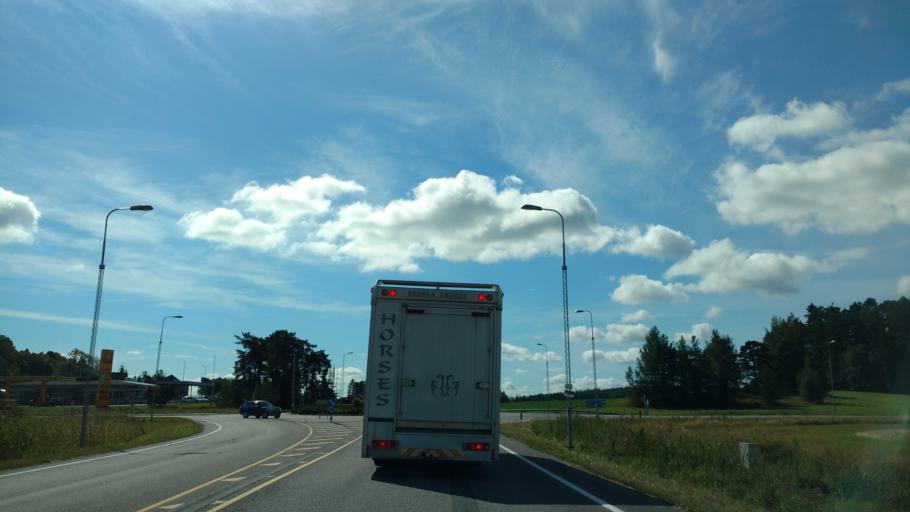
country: FI
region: Varsinais-Suomi
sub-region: Salo
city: Pernioe
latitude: 60.2062
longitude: 23.1115
